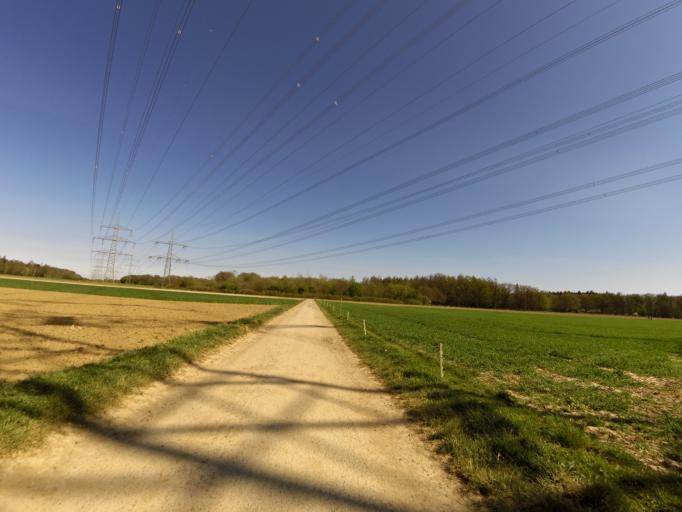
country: DE
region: North Rhine-Westphalia
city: Meckenheim
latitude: 50.6596
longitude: 7.0085
